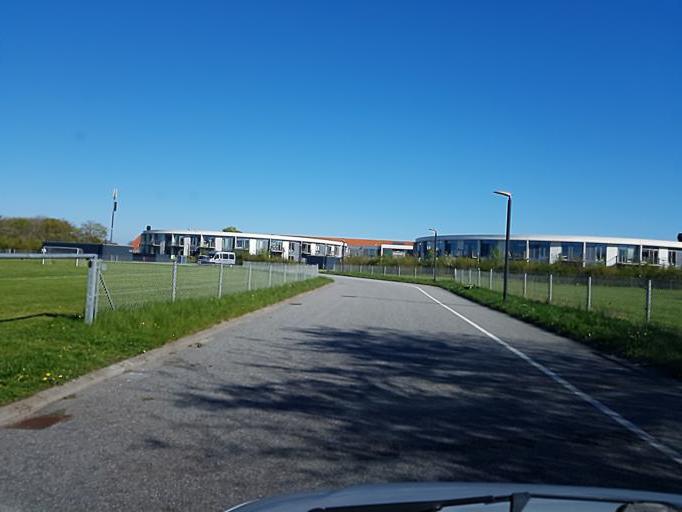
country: DK
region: South Denmark
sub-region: Fano Kommune
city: Nordby
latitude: 55.5008
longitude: 8.4023
